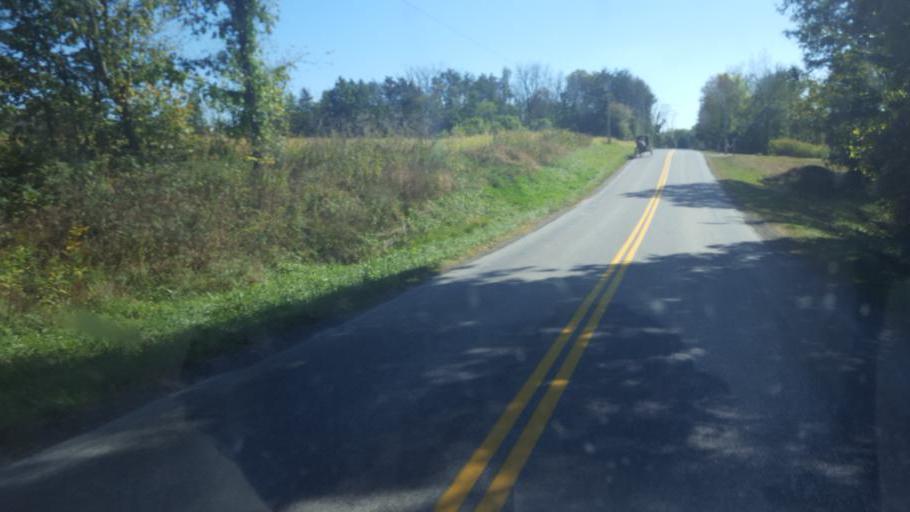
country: US
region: Ohio
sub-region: Wayne County
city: West Salem
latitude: 40.9243
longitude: -82.1618
